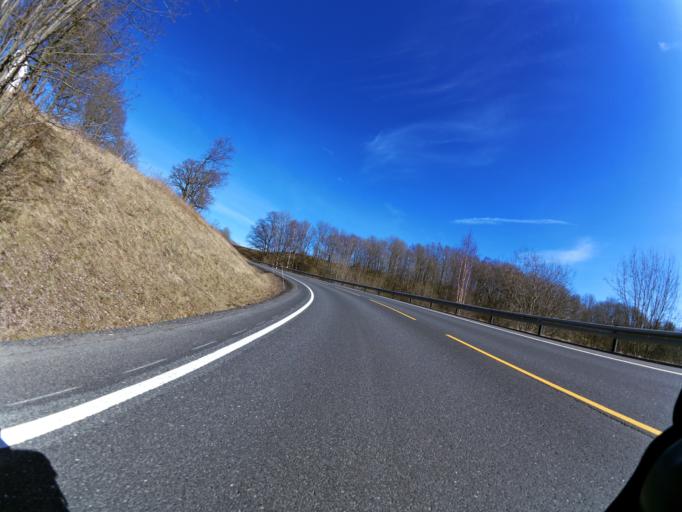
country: NO
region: Ostfold
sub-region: Rade
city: Karlshus
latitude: 59.3247
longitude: 10.9639
